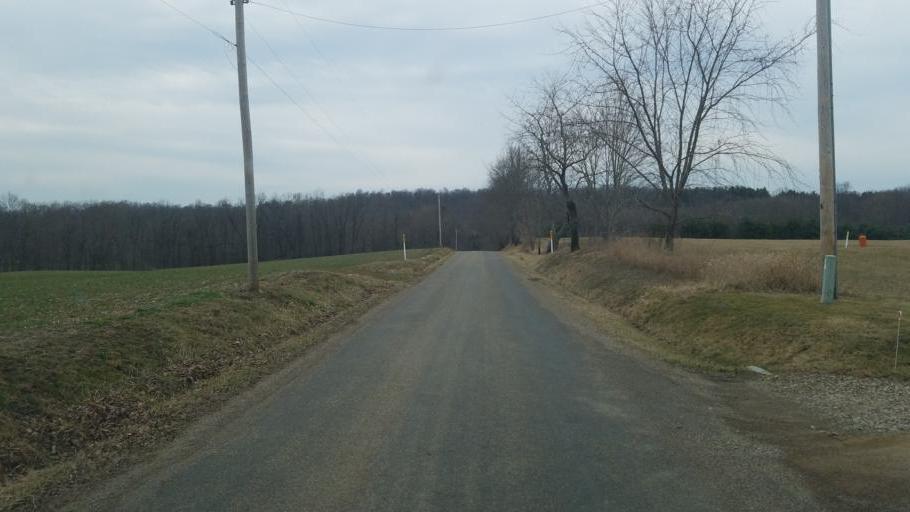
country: US
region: Ohio
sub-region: Ashland County
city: Loudonville
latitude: 40.7192
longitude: -82.3415
